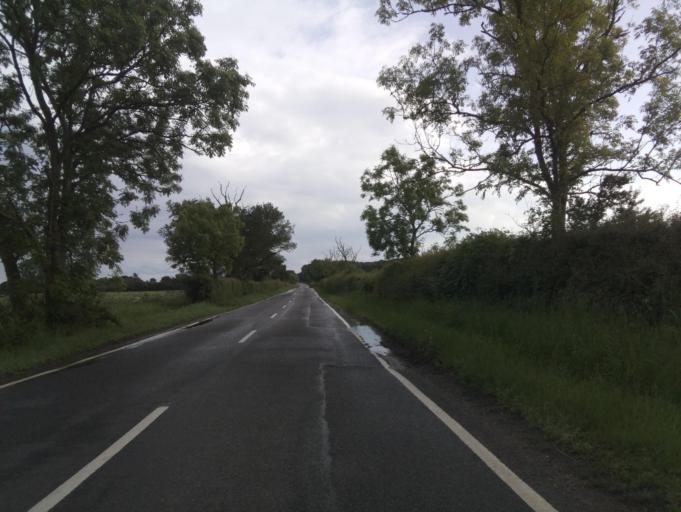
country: GB
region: England
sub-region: Lincolnshire
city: Great Gonerby
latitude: 53.0054
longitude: -0.6665
